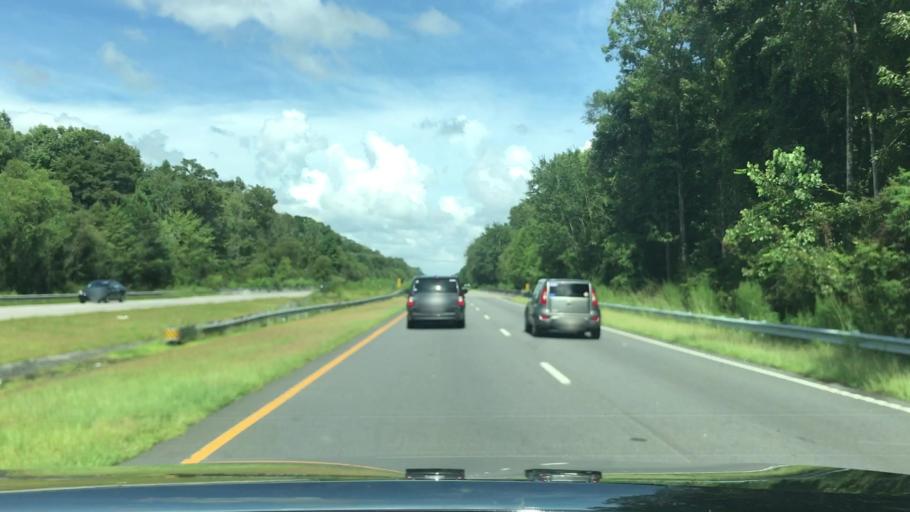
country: US
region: South Carolina
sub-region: Jasper County
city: Hardeeville
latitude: 32.3072
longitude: -81.0077
